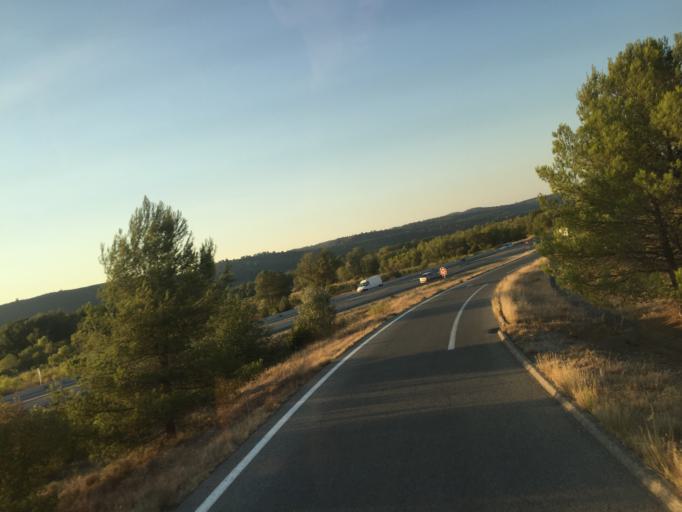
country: FR
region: Provence-Alpes-Cote d'Azur
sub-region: Departement du Vaucluse
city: Beaumont-de-Pertuis
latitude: 43.7046
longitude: 5.7316
